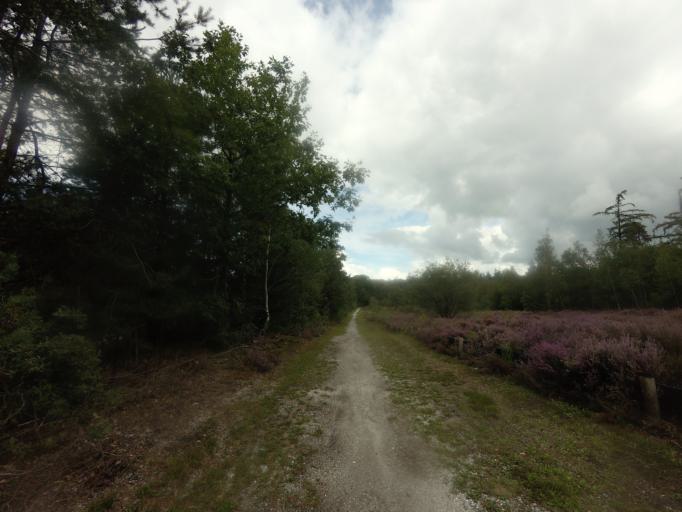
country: NL
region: Overijssel
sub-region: Gemeente Staphorst
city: Staphorst
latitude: 52.6356
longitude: 6.2733
